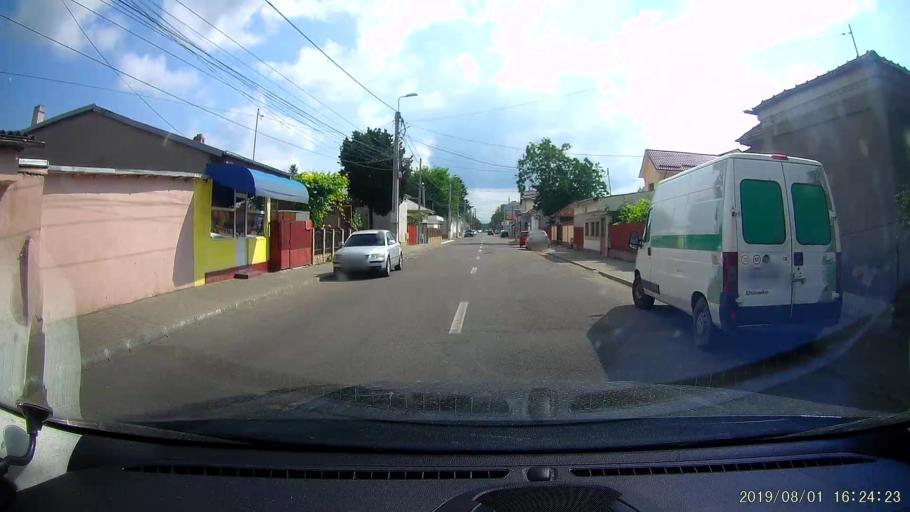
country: RO
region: Calarasi
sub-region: Municipiul Calarasi
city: Calarasi
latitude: 44.1962
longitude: 27.3299
